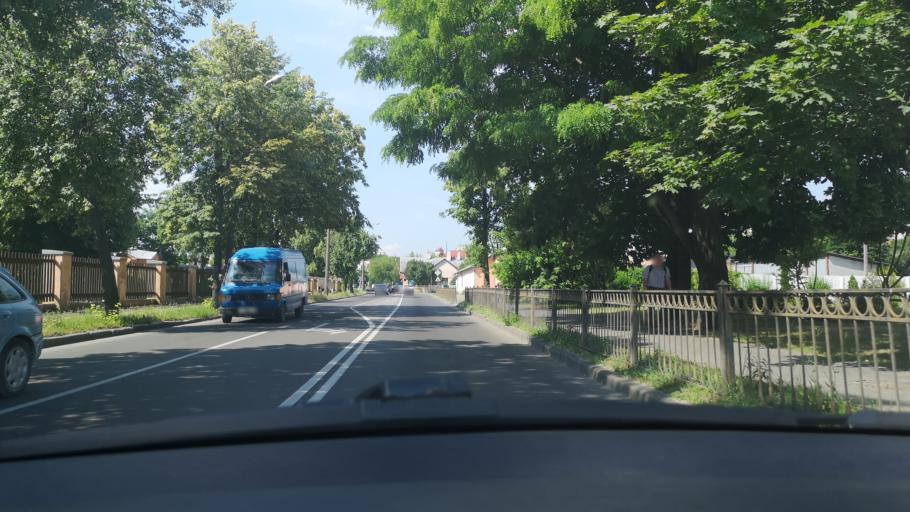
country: BY
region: Brest
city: Brest
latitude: 52.1015
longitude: 23.7048
